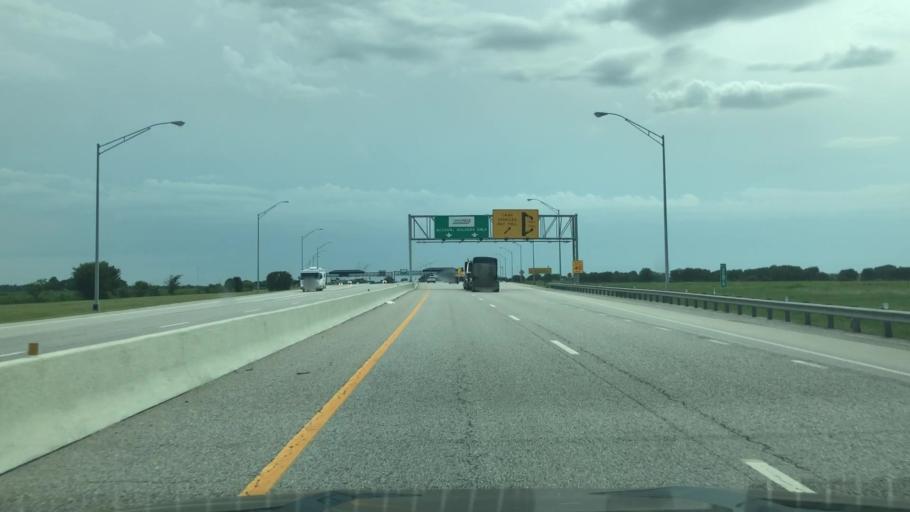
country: US
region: Oklahoma
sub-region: Craig County
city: Vinita
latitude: 36.6082
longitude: -95.1828
